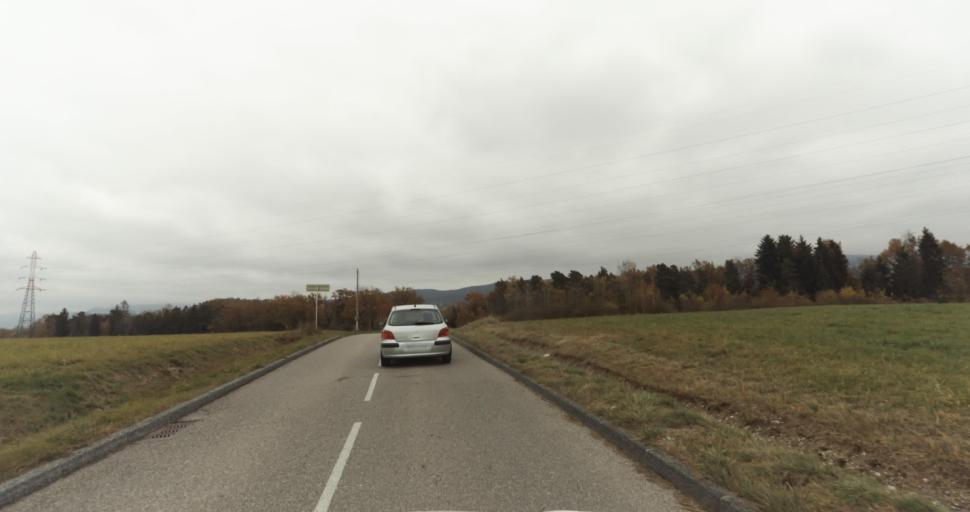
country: FR
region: Rhone-Alpes
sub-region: Departement de la Haute-Savoie
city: Seynod
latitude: 45.8747
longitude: 6.0642
